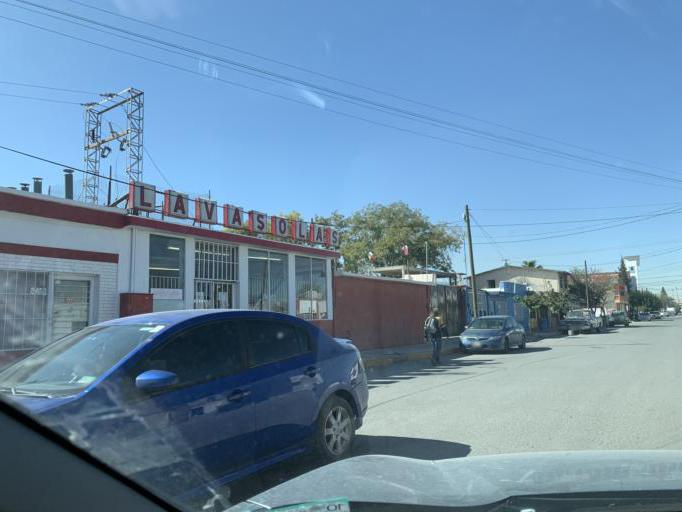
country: MX
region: Chihuahua
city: Ciudad Juarez
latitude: 31.7233
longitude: -106.4629
